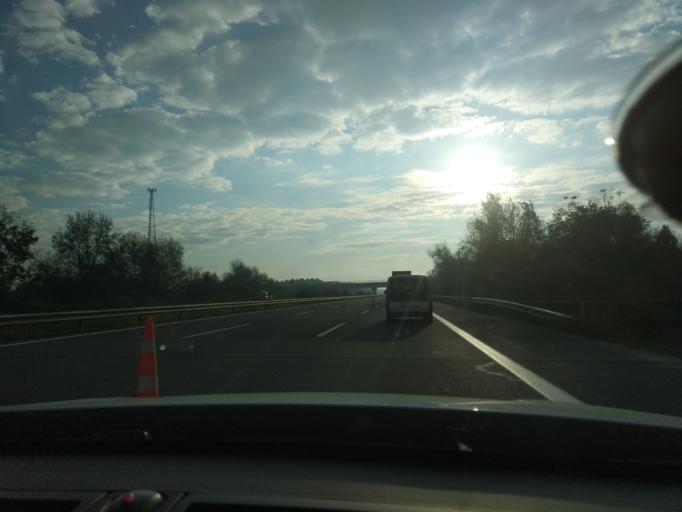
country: TR
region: Duzce
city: Duzce
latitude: 40.8119
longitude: 31.1129
